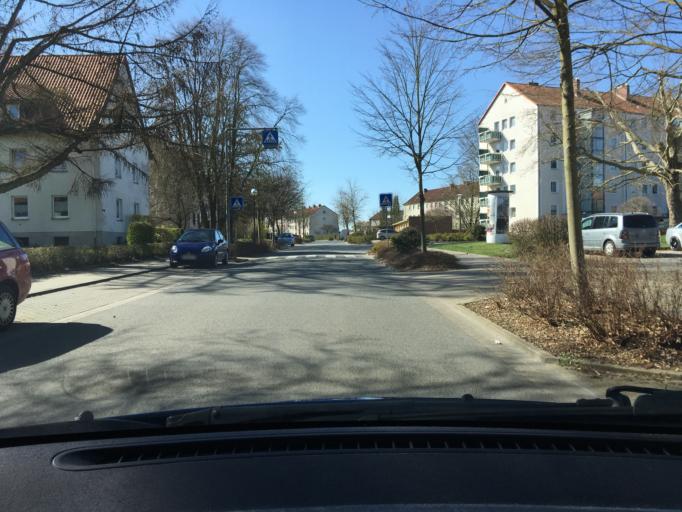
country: DE
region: Lower Saxony
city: Uelzen
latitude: 52.9660
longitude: 10.5399
